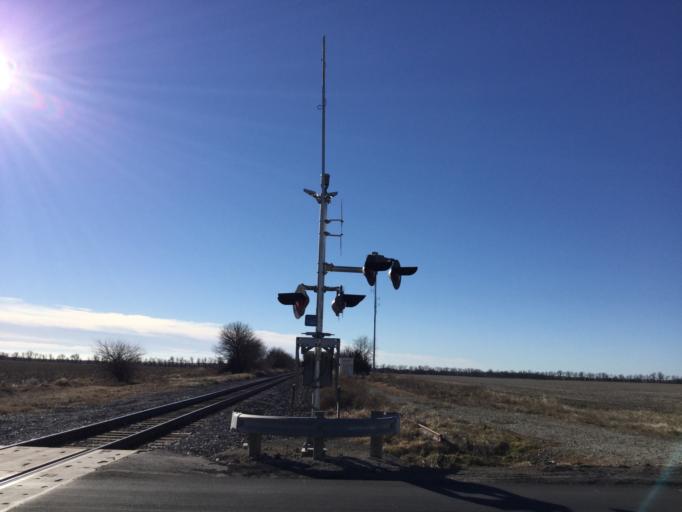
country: US
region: Kansas
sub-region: Marion County
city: Peabody
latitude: 38.0438
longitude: -97.1253
